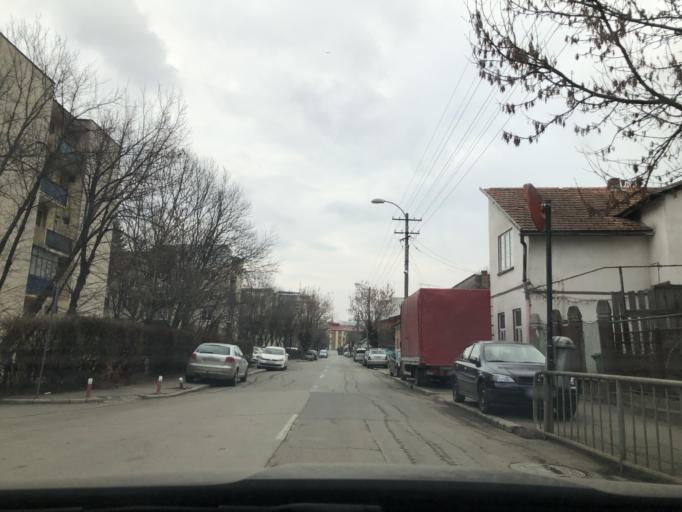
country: RO
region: Cluj
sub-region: Municipiul Cluj-Napoca
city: Cluj-Napoca
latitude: 46.7635
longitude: 23.5658
